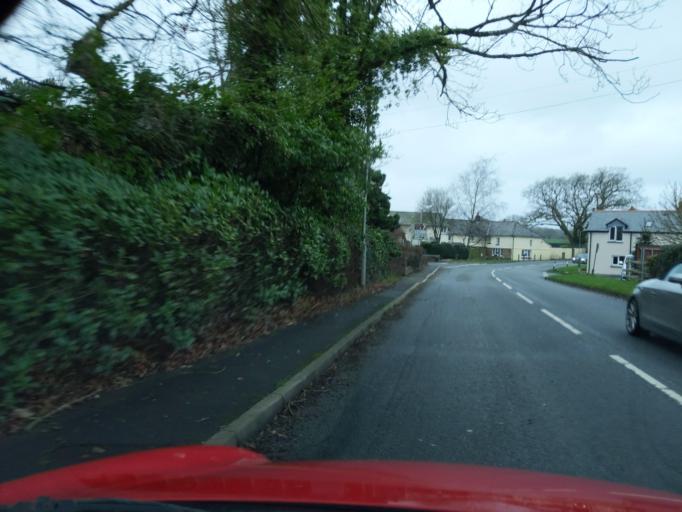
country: GB
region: England
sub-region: Devon
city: Holsworthy
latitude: 50.7690
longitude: -4.3368
